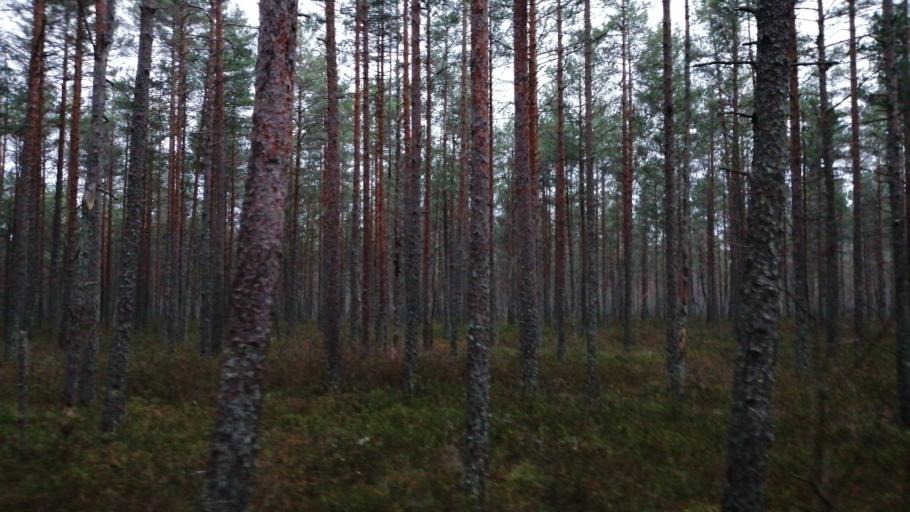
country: EE
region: Polvamaa
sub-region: Polva linn
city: Polva
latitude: 58.1549
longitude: 27.0631
